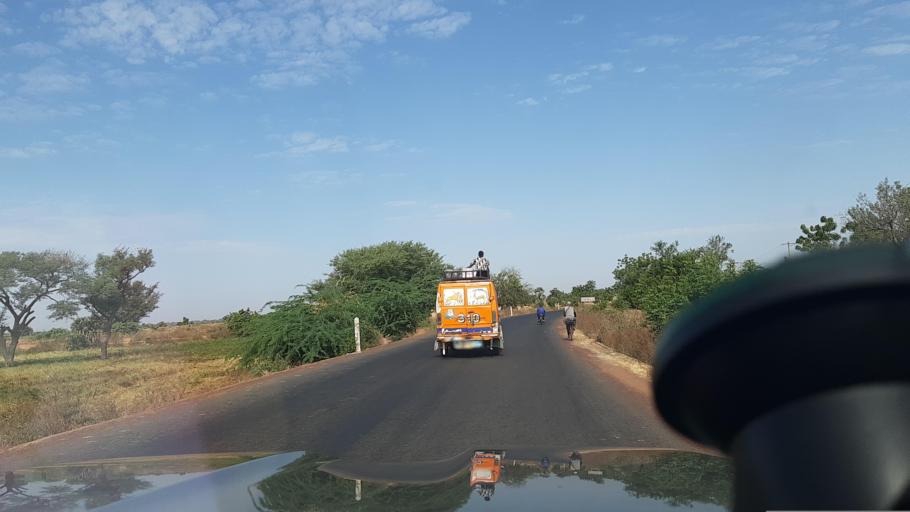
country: ML
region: Segou
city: Markala
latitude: 13.6867
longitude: -6.0993
